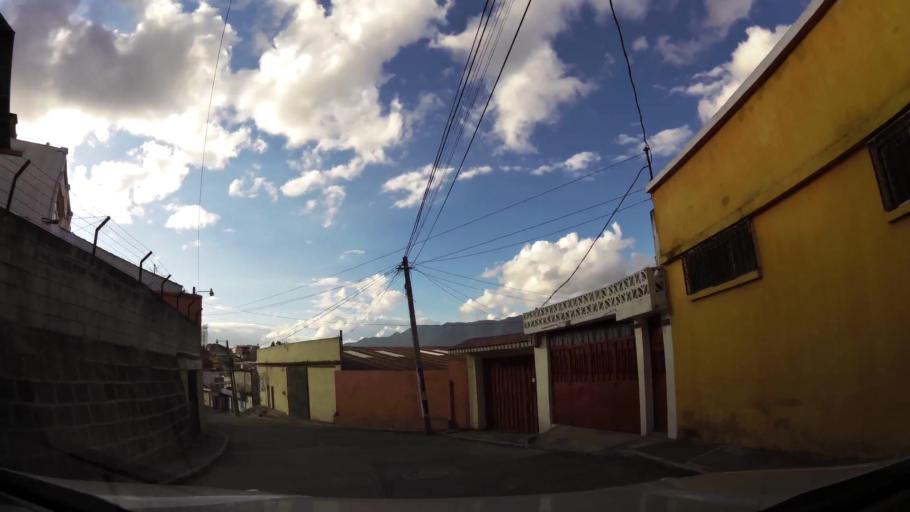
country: GT
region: Quetzaltenango
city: Quetzaltenango
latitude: 14.8519
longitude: -91.5243
